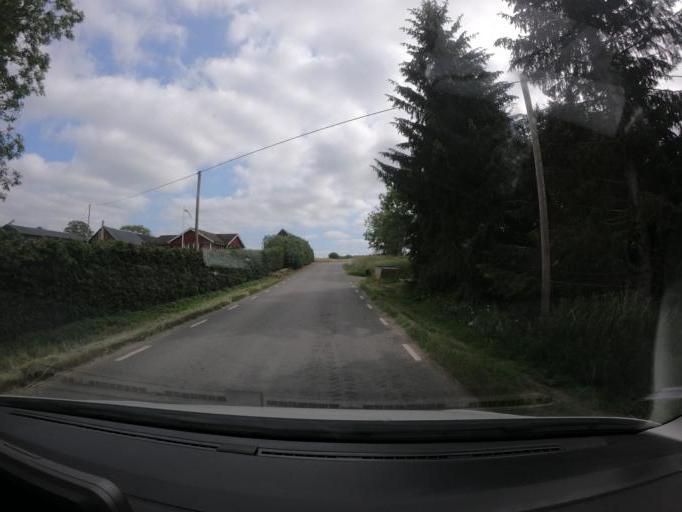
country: SE
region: Skane
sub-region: Hassleholms Kommun
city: Tormestorp
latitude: 56.1481
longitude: 13.6283
